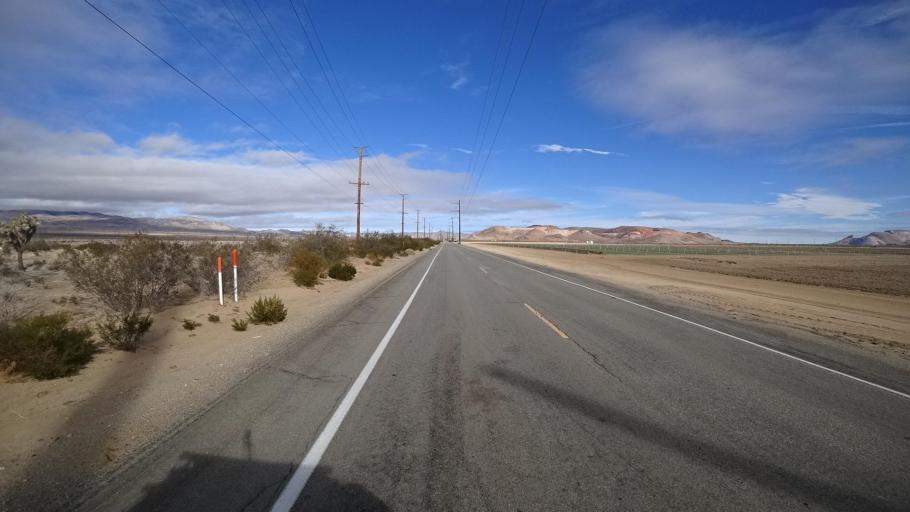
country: US
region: California
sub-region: Kern County
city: Rosamond
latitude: 34.9332
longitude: -118.2903
